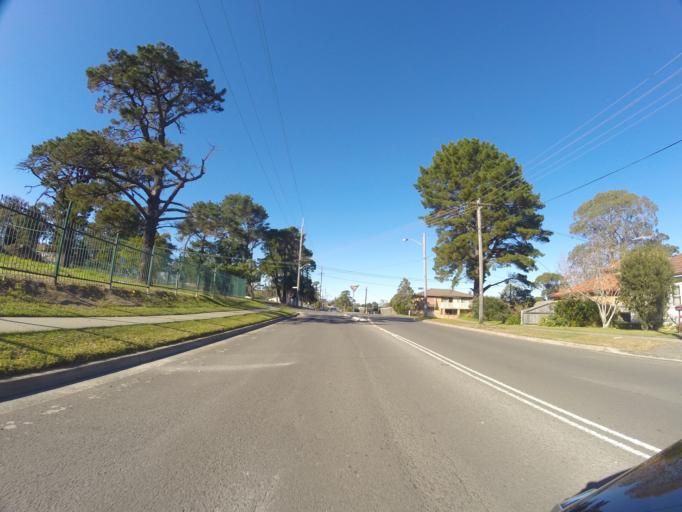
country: AU
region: New South Wales
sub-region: Sutherland Shire
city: Engadine
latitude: -34.0659
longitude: 151.0053
